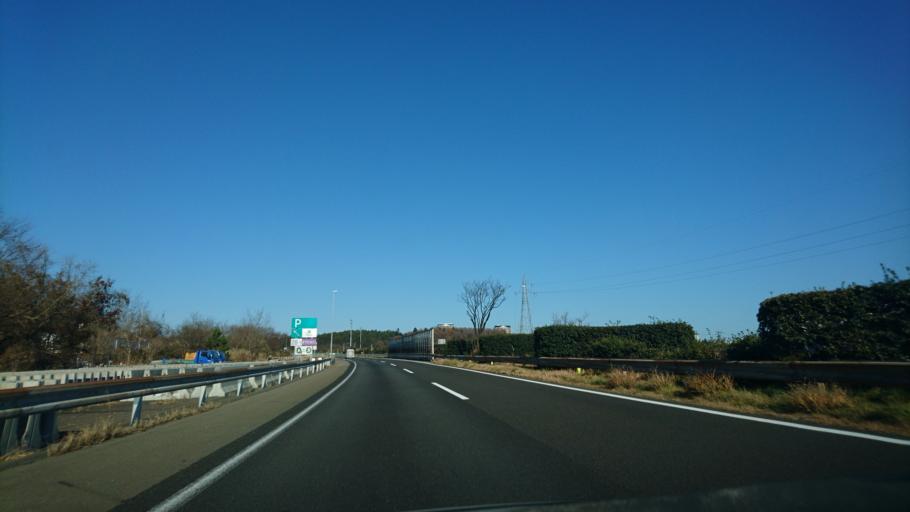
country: JP
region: Miyagi
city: Sendai-shi
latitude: 38.3263
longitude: 140.8539
